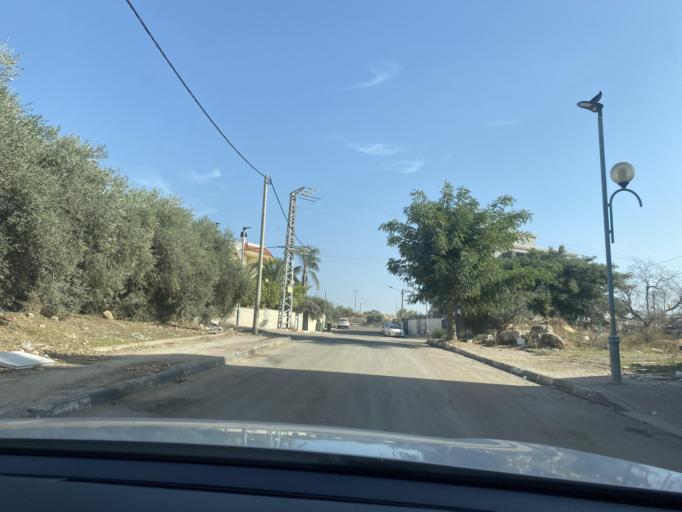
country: IL
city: Oranit
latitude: 32.1329
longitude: 34.9741
